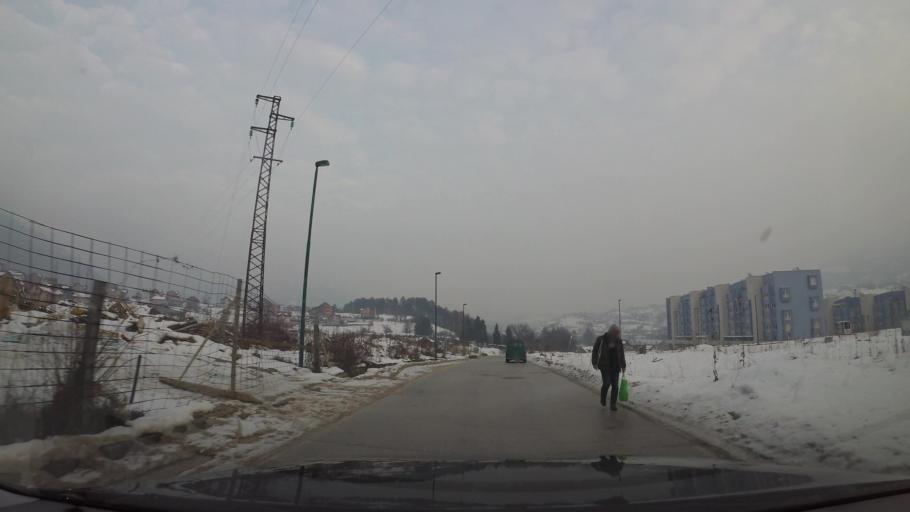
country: BA
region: Federation of Bosnia and Herzegovina
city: Vogosca
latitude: 43.9015
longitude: 18.3531
